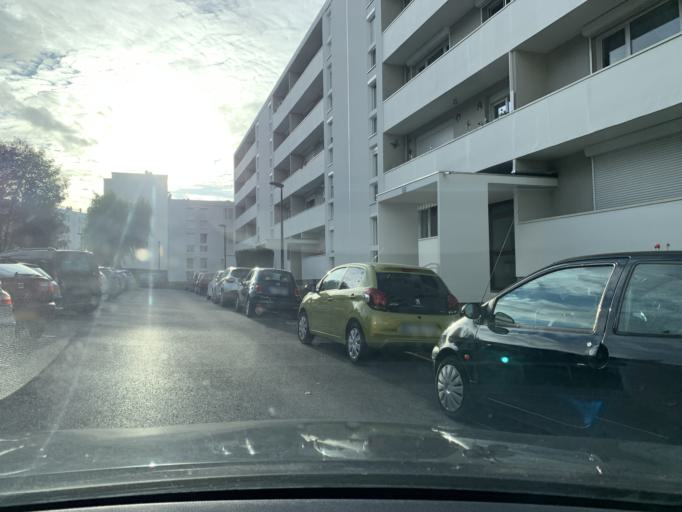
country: FR
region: Picardie
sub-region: Departement de l'Aisne
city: Harly
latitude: 49.8576
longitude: 3.3080
